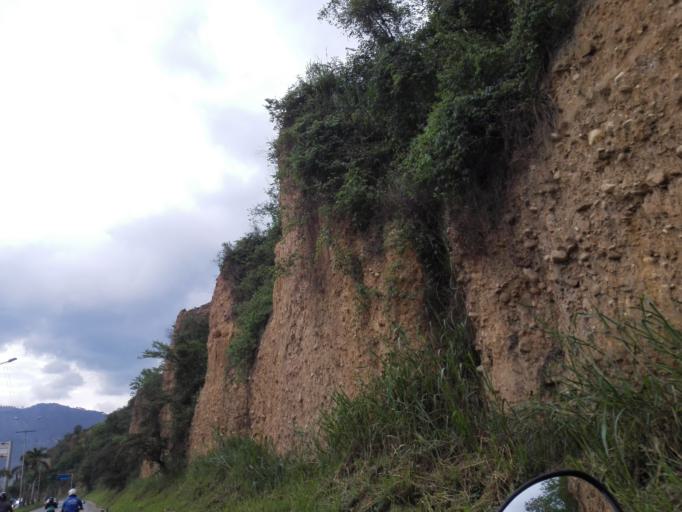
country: CO
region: Santander
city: Giron
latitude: 7.0840
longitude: -73.1509
